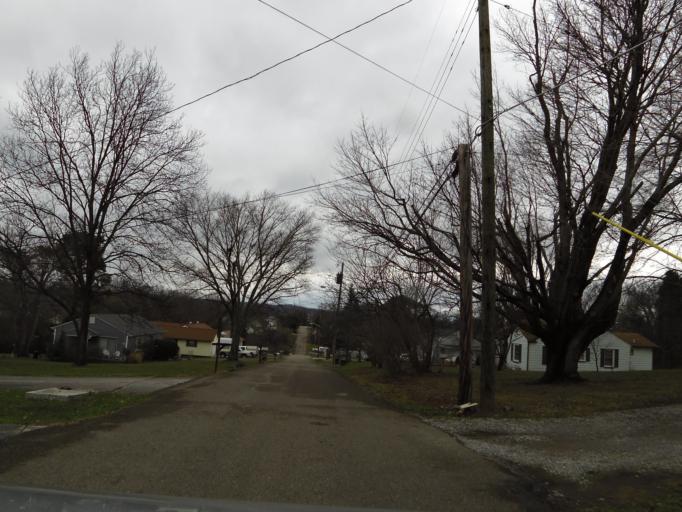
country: US
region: Tennessee
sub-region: Knox County
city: Knoxville
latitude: 35.9975
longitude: -83.9756
